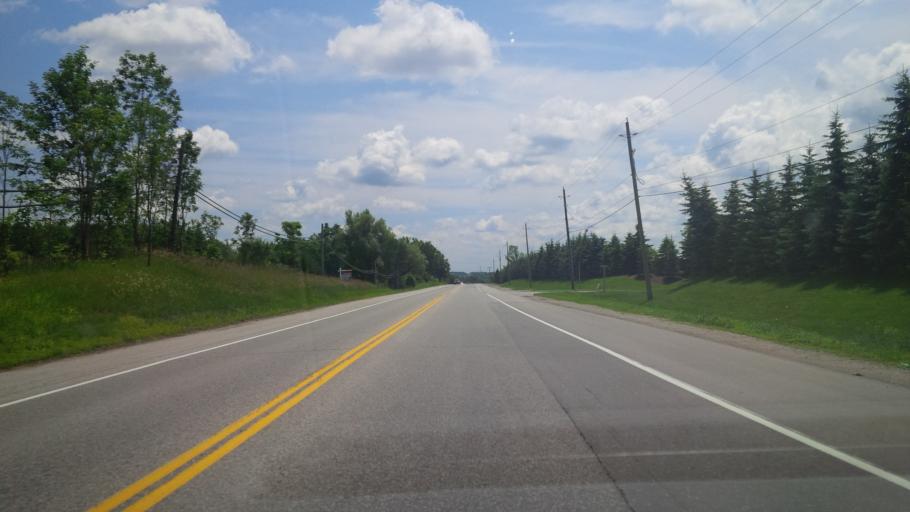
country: CA
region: Ontario
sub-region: Wellington County
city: Guelph
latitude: 43.4846
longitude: -80.1676
